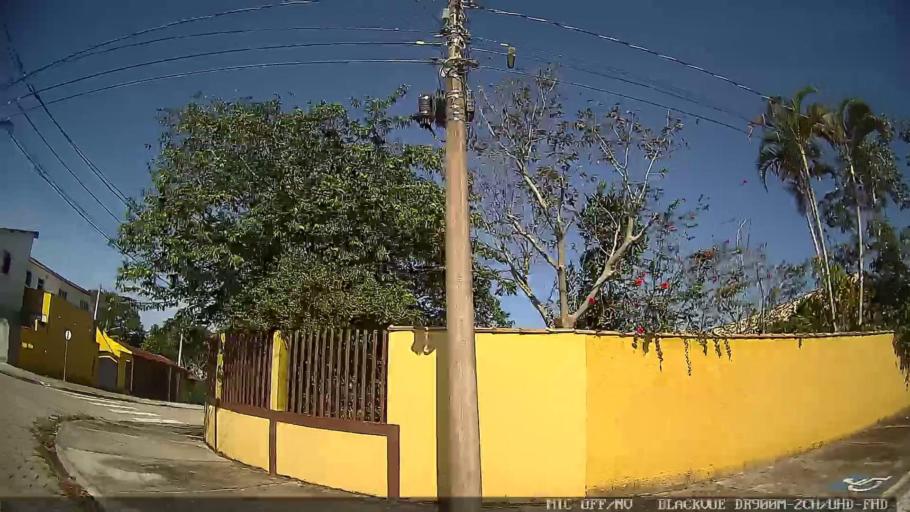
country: BR
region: Sao Paulo
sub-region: Itanhaem
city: Itanhaem
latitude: -24.2137
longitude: -46.8639
